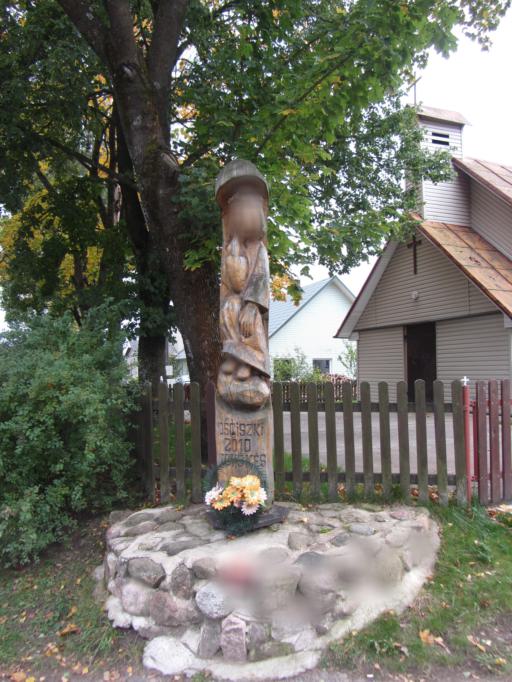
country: LT
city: Nemencine
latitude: 54.7708
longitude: 25.6666
